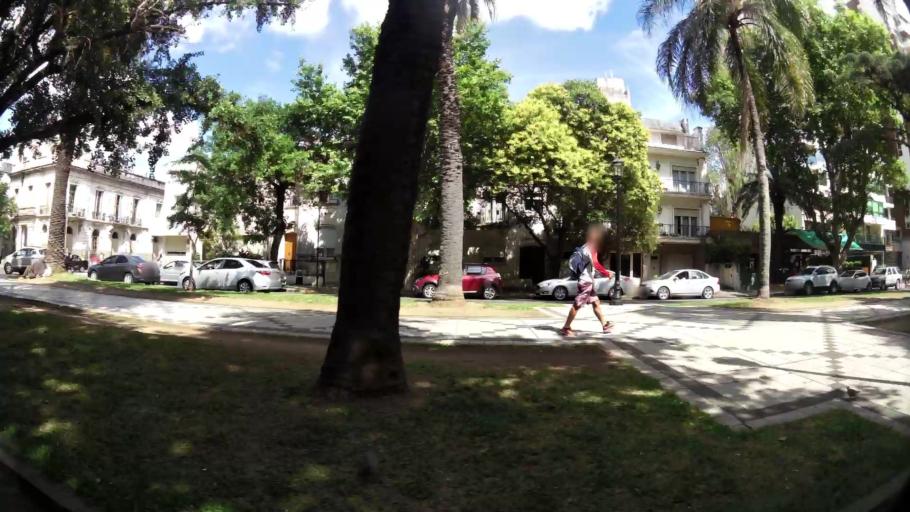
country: AR
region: Santa Fe
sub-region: Departamento de Rosario
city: Rosario
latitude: -32.9388
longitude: -60.6520
